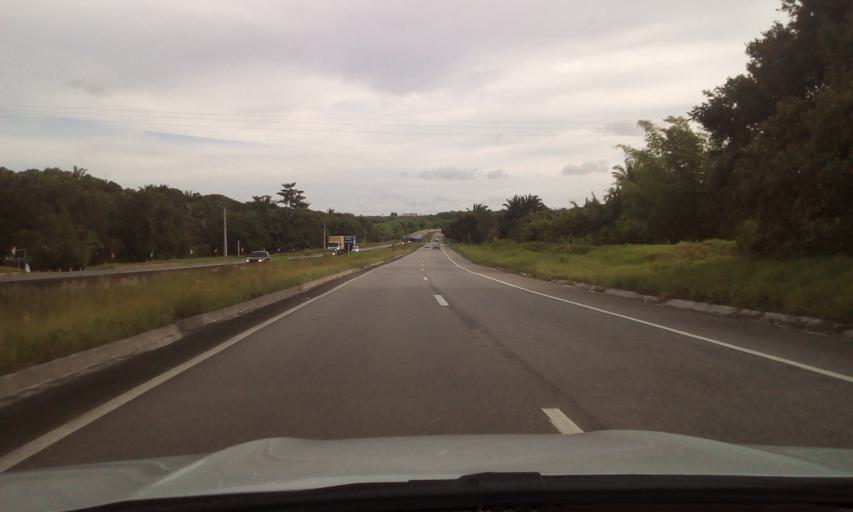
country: BR
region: Paraiba
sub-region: Alhandra
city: Alhandra
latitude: -7.4030
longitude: -34.9549
